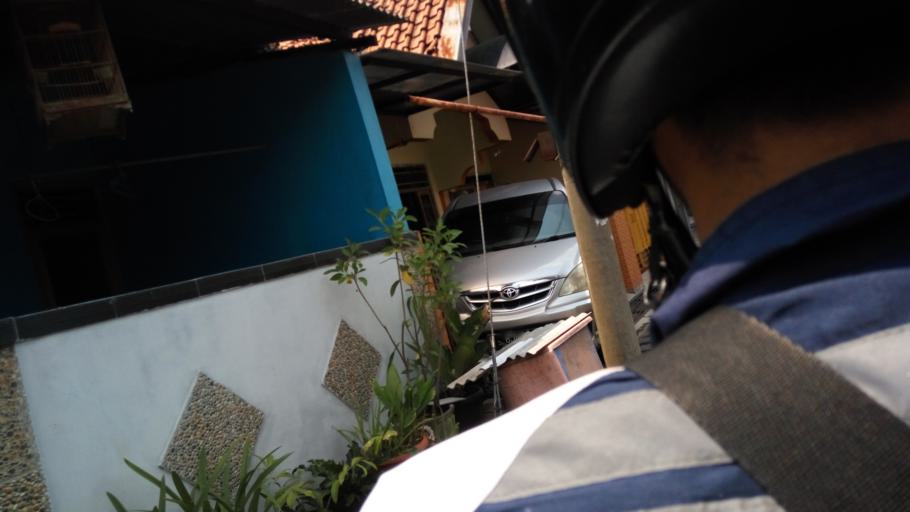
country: ID
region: Central Java
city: Mranggen
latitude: -7.0447
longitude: 110.4739
